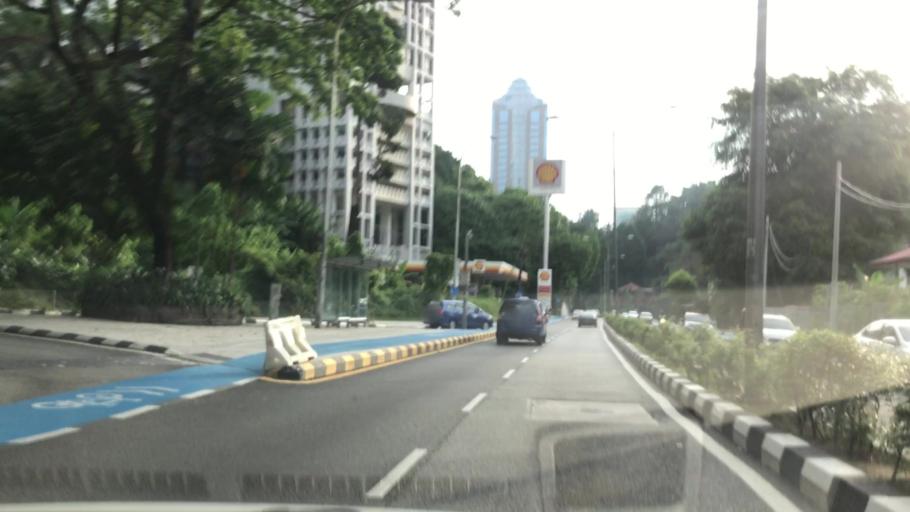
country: MY
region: Kuala Lumpur
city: Kuala Lumpur
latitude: 3.1503
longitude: 101.7052
